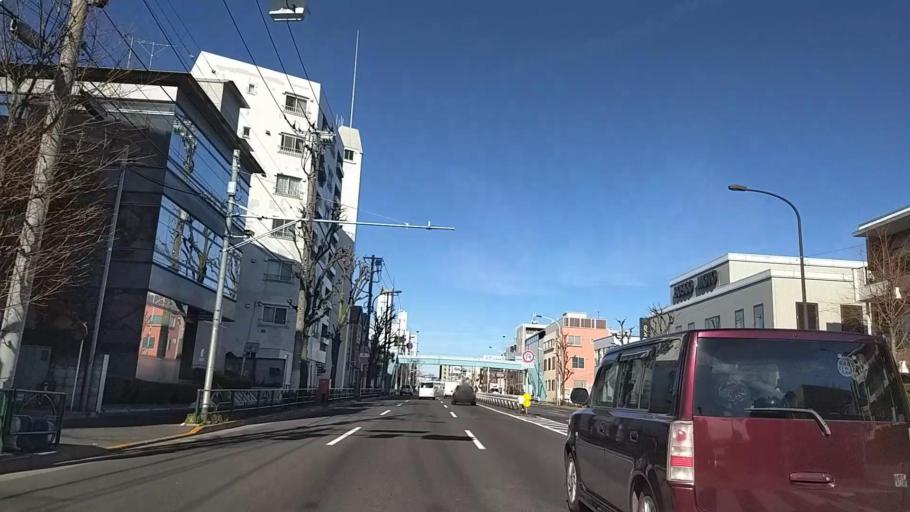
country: JP
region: Kanagawa
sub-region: Kawasaki-shi
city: Kawasaki
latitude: 35.5957
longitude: 139.6728
